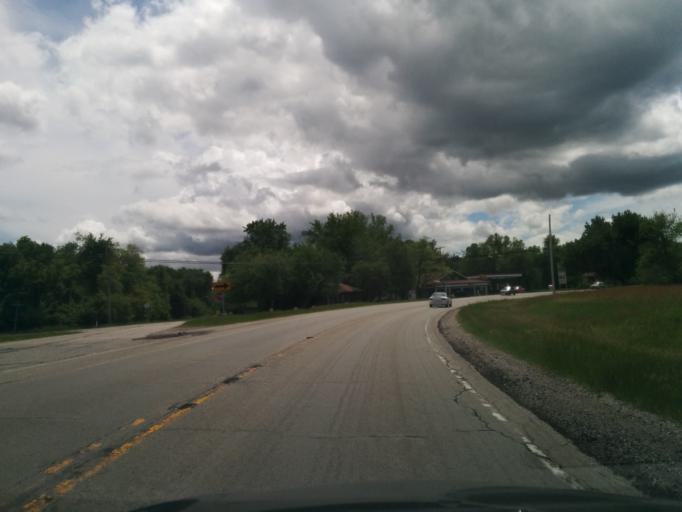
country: US
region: Indiana
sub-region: LaPorte County
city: Michigan City
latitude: 41.6964
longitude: -86.9326
